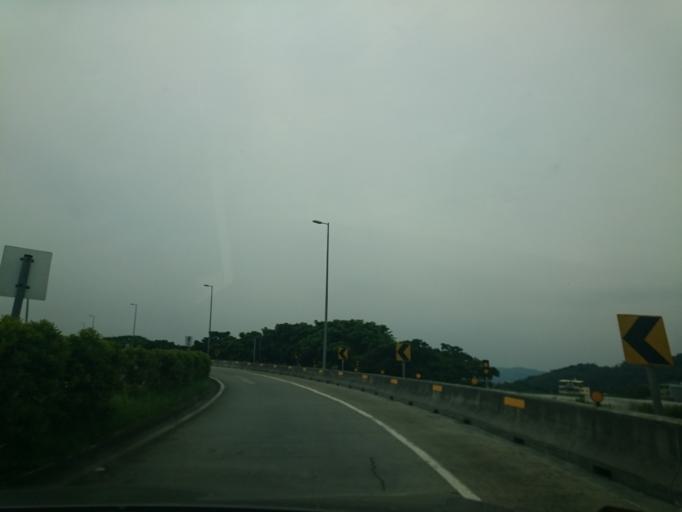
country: TW
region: Taiwan
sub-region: Nantou
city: Nantou
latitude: 23.8538
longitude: 120.7037
